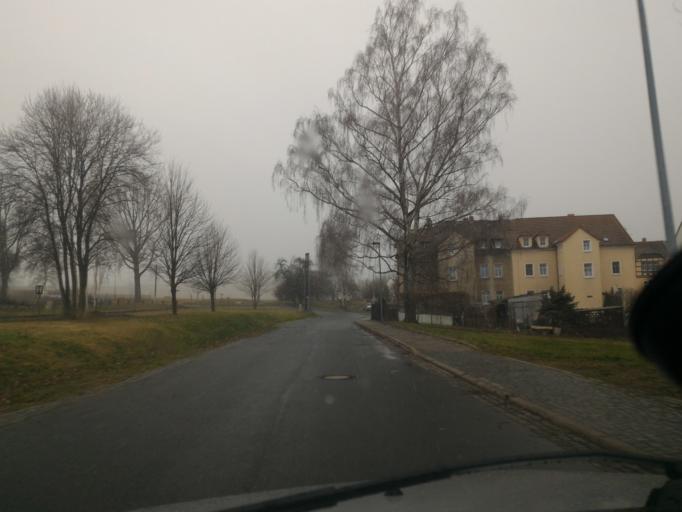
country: DE
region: Saxony
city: Olbersdorf
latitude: 50.8810
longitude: 14.7807
